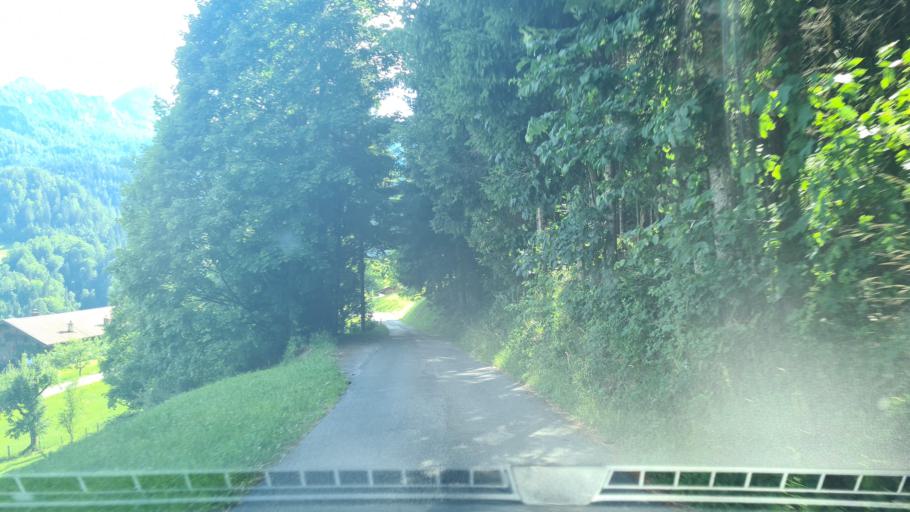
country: AT
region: Salzburg
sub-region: Politischer Bezirk Zell am See
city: Unken
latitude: 47.6504
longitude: 12.7078
